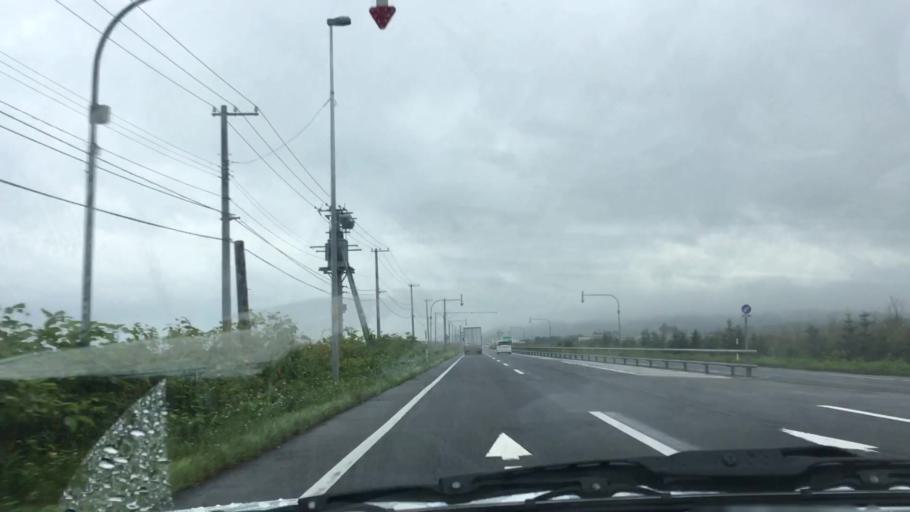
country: JP
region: Hokkaido
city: Niseko Town
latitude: 42.4003
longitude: 140.3030
